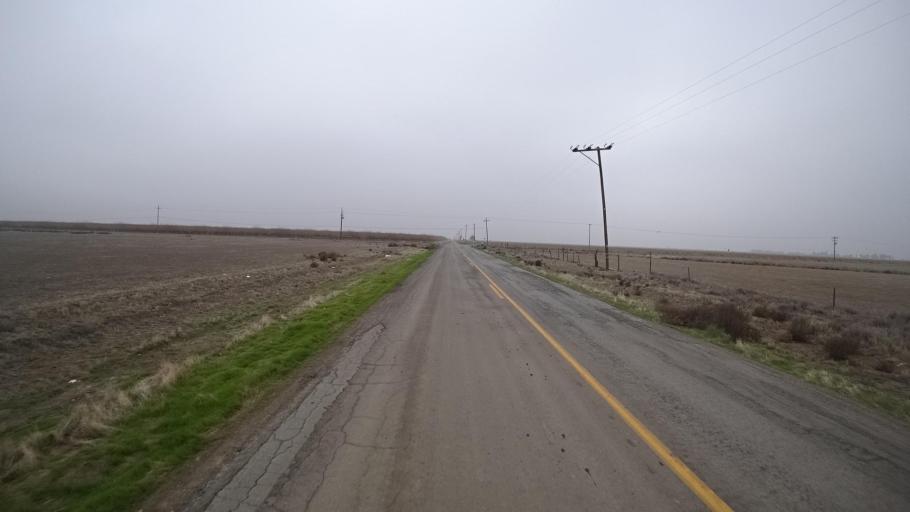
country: US
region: California
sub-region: Tulare County
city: Alpaugh
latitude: 35.7041
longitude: -119.4906
